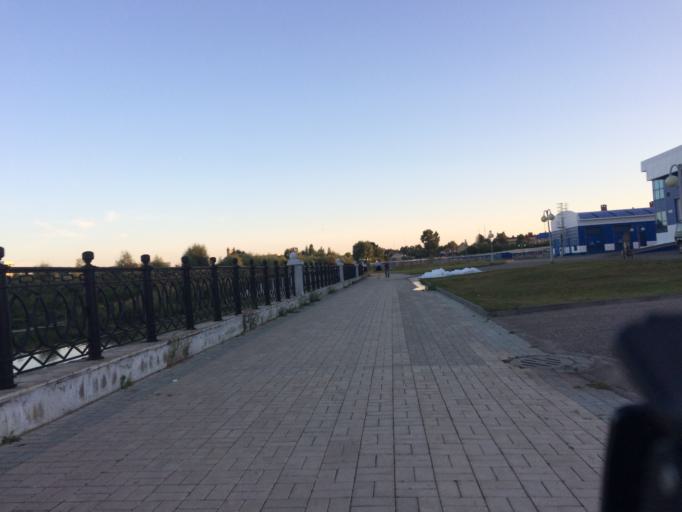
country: RU
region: Mariy-El
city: Yoshkar-Ola
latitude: 56.6246
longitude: 47.8962
